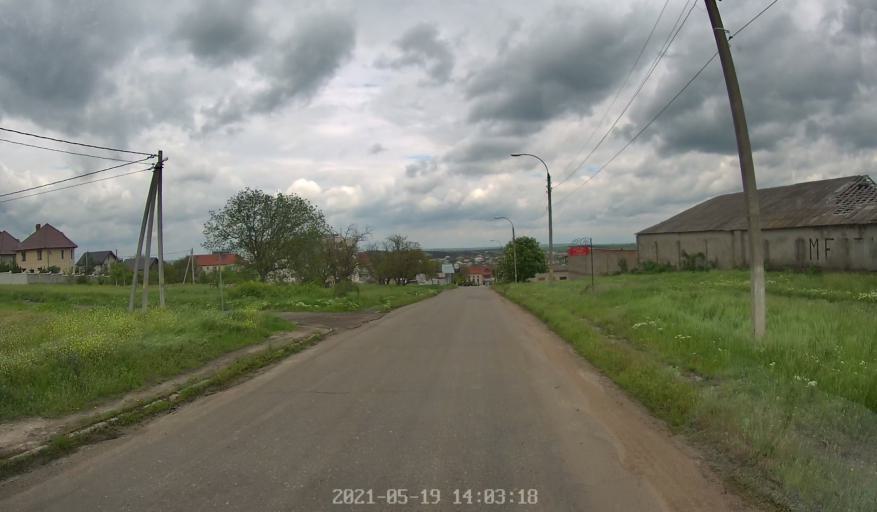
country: MD
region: Chisinau
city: Chisinau
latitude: 47.0373
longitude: 28.9498
